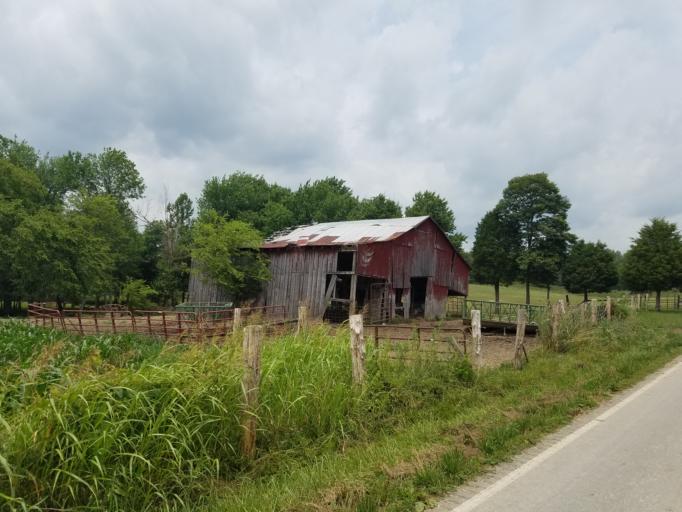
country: US
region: Kentucky
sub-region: Hart County
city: Munfordville
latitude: 37.3636
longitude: -86.0948
